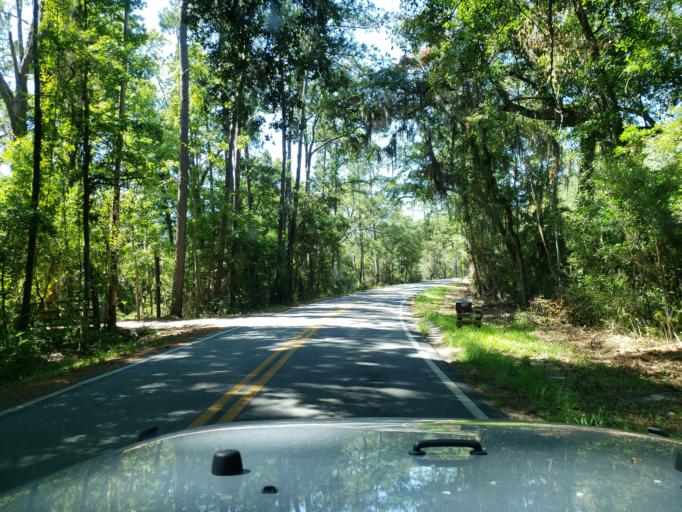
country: US
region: Georgia
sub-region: Chatham County
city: Georgetown
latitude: 31.9684
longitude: -81.2184
